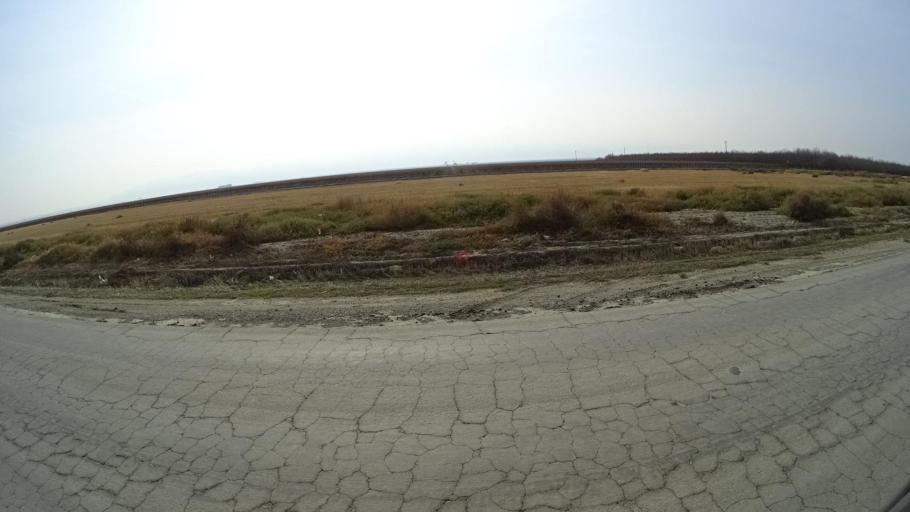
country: US
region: California
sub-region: Kern County
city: Greenfield
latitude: 35.0948
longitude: -119.0815
